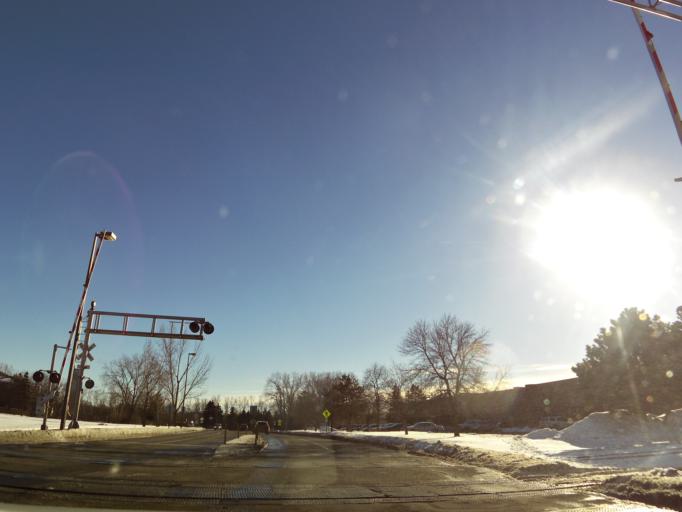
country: US
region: Minnesota
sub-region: Hennepin County
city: Saint Louis Park
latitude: 44.9437
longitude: -93.3403
